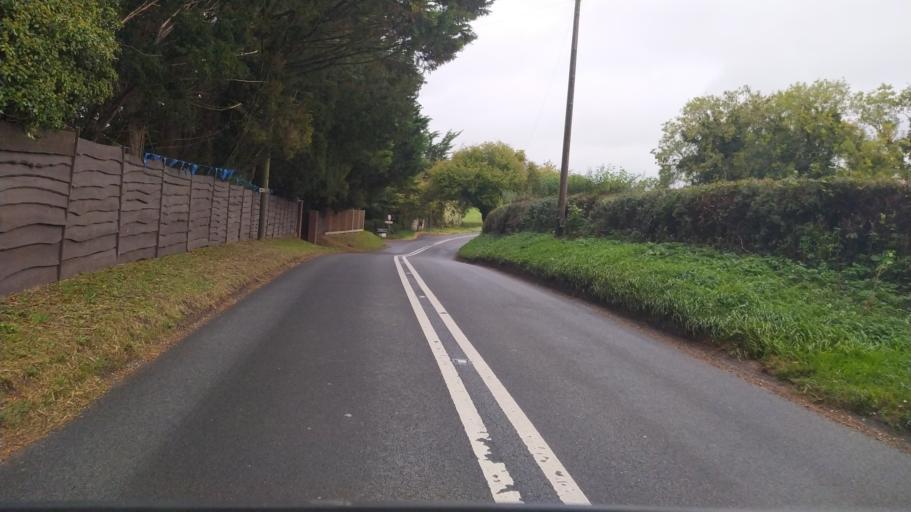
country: GB
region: England
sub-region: Wiltshire
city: Salisbury
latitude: 51.1015
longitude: -1.7570
